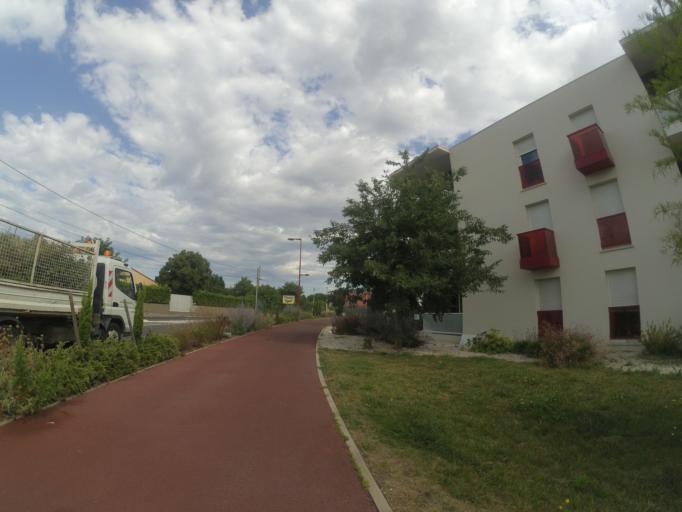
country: FR
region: Languedoc-Roussillon
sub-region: Departement des Pyrenees-Orientales
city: Toulouges
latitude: 42.6736
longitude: 2.8263
